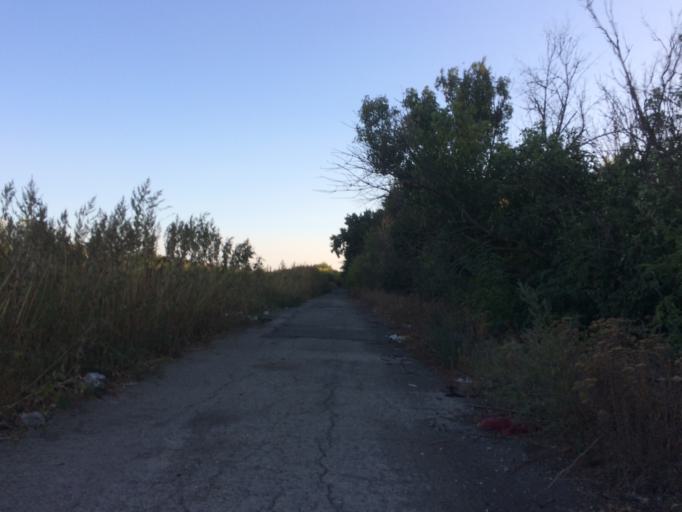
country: RU
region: Rostov
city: Gigant
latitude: 46.5166
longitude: 41.1947
